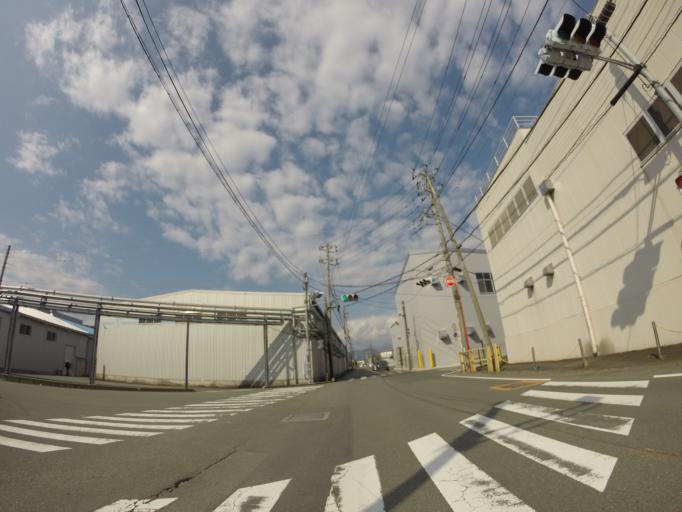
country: JP
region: Shizuoka
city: Fujinomiya
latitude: 35.1980
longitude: 138.6397
